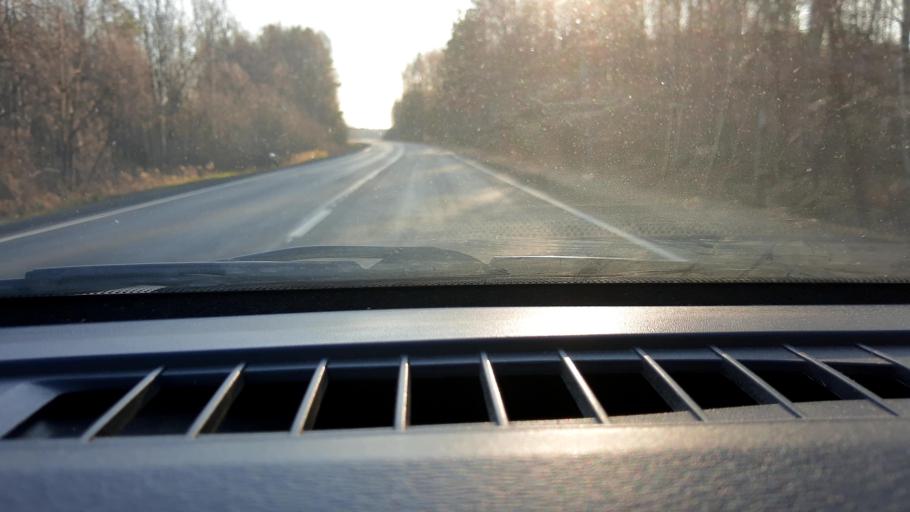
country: RU
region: Nizjnij Novgorod
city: Novaya Balakhna
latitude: 56.5514
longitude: 43.7481
